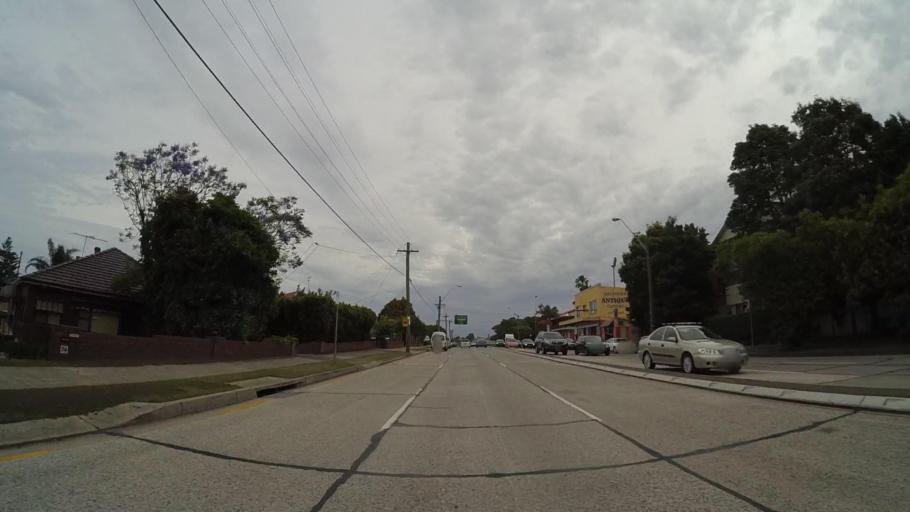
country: AU
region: New South Wales
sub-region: Kogarah
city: Beverly Park
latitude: -33.9720
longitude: 151.1318
